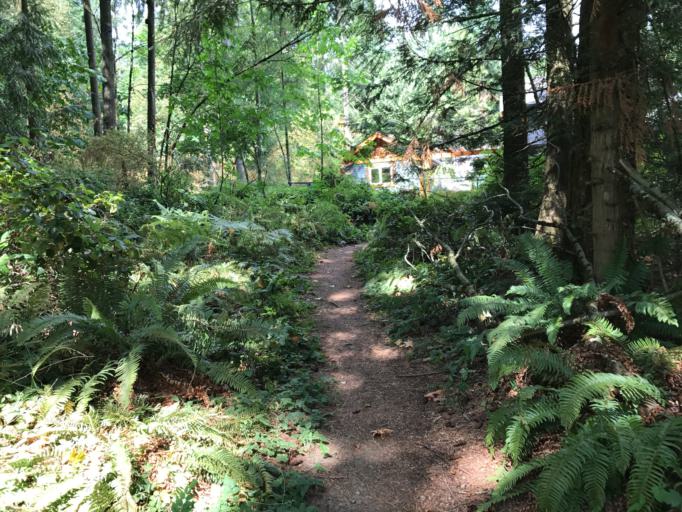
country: CA
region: British Columbia
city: North Cowichan
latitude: 48.9253
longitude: -123.7374
